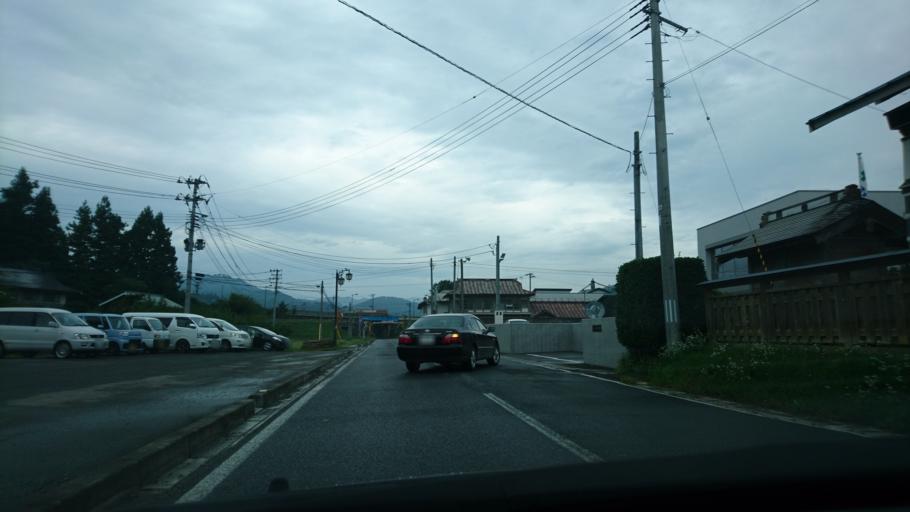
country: JP
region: Iwate
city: Ichinoseki
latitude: 38.9856
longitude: 141.2475
